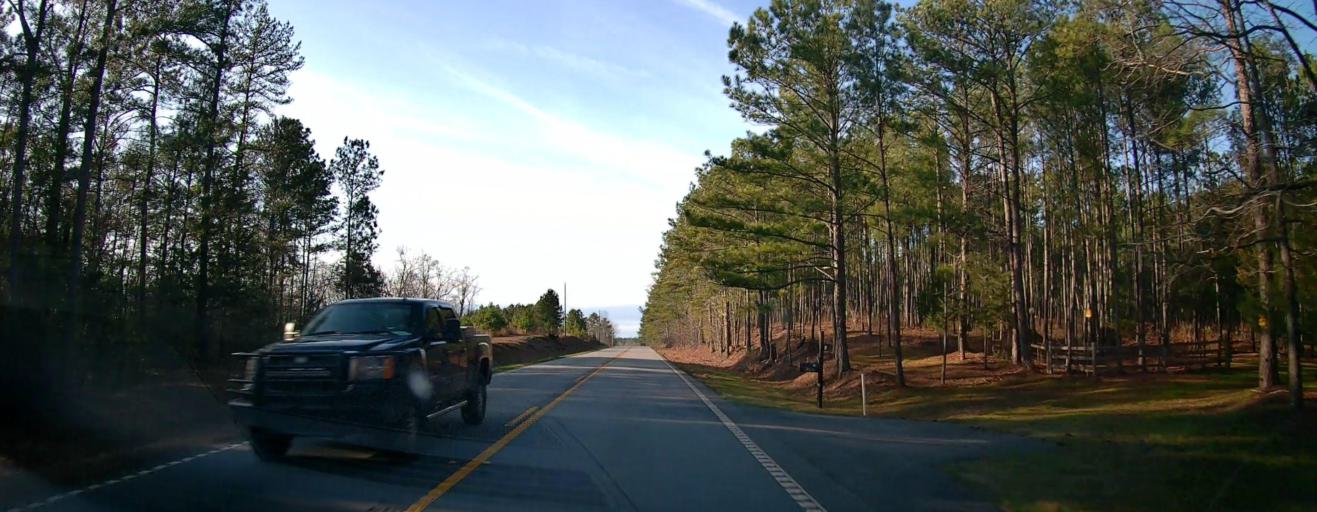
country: US
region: Alabama
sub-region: Chambers County
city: Valley
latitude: 32.7882
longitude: -85.0983
